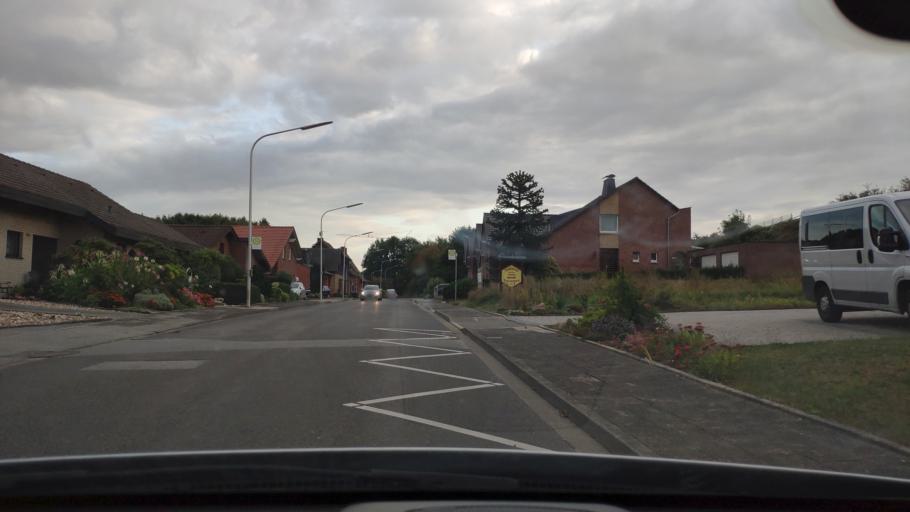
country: DE
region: North Rhine-Westphalia
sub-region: Regierungsbezirk Koln
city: Heinsberg
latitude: 51.0529
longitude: 6.1245
